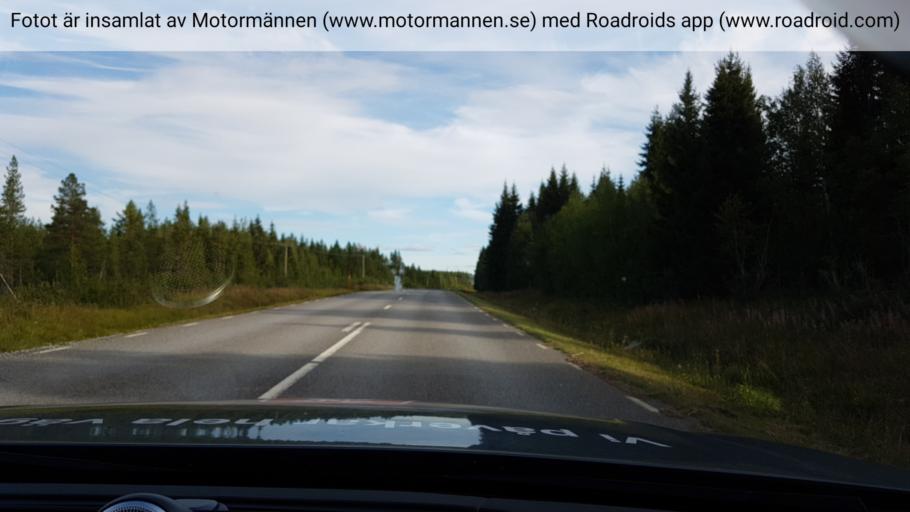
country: SE
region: Jaemtland
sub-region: Stroemsunds Kommun
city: Stroemsund
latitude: 64.2676
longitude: 15.3900
